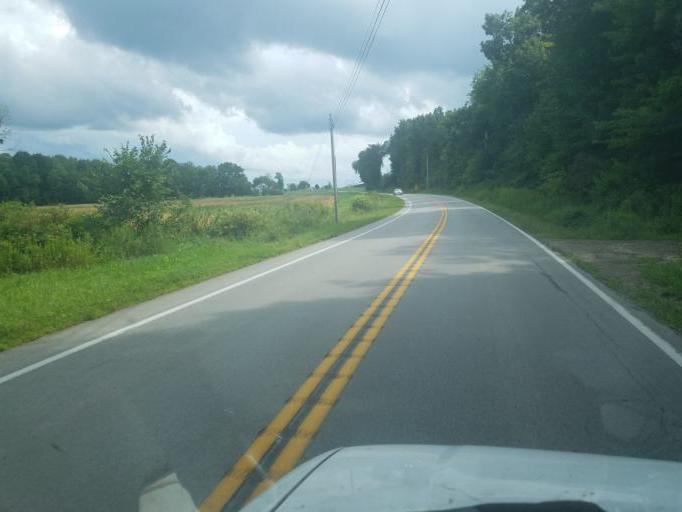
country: US
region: Pennsylvania
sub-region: Crawford County
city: Conneaut Lakeshore
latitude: 41.5882
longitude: -80.3032
